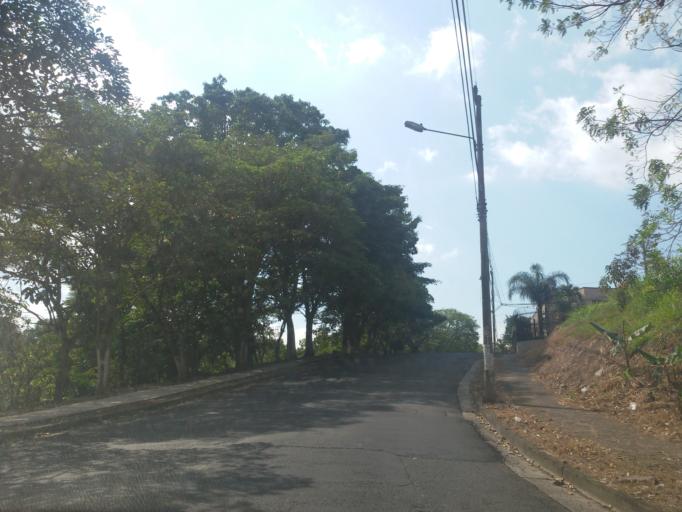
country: CR
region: San Jose
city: Curridabat
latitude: 9.9079
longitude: -84.0319
